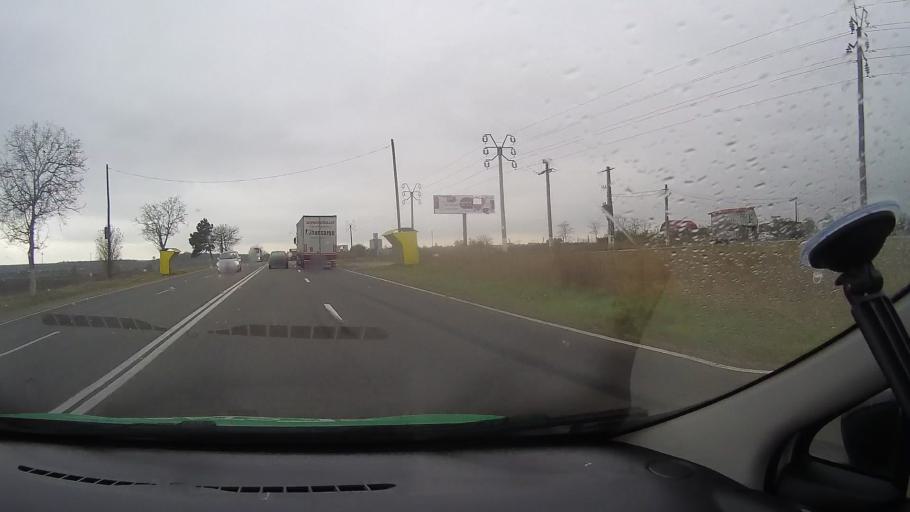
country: RO
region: Constanta
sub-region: Comuna Valu lui Traian
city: Valu lui Traian
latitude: 44.1657
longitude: 28.5229
